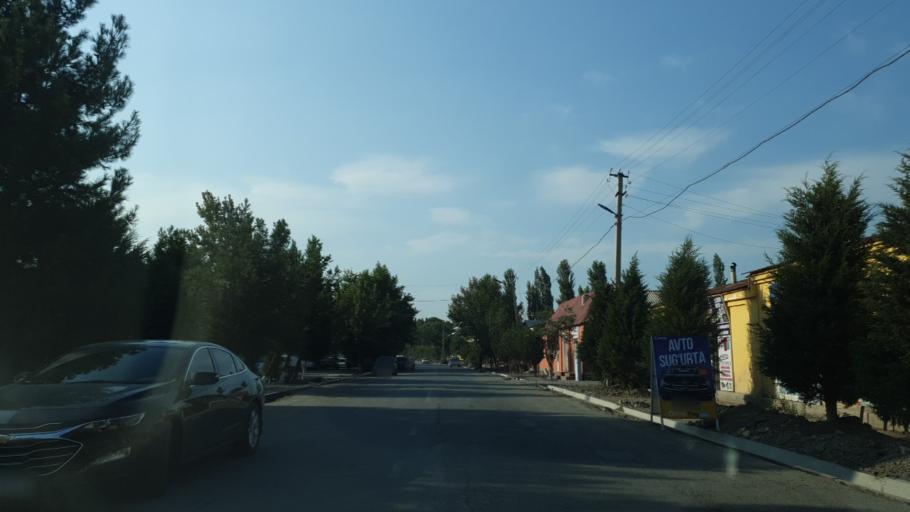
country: UZ
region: Fergana
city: Yaypan
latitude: 40.3751
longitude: 70.8123
